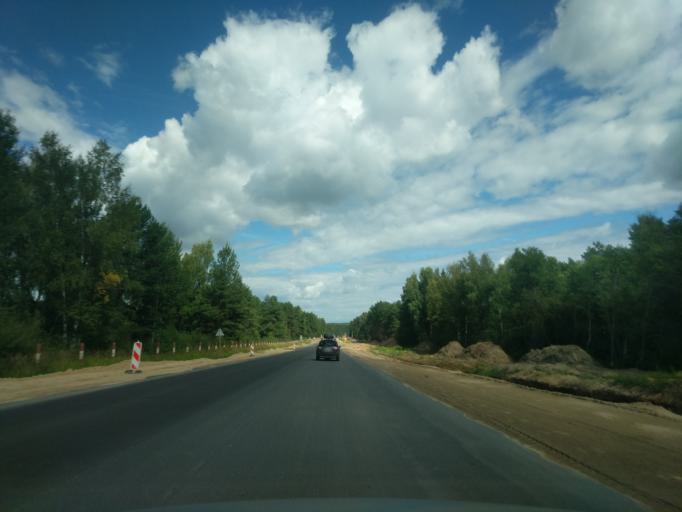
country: RU
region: Jaroslavl
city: Levashevo
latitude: 57.6644
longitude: 40.5729
